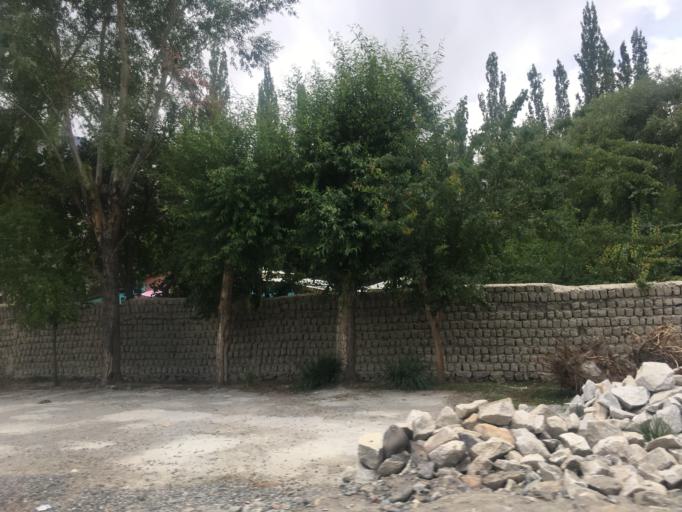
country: PK
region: Gilgit-Baltistan
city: Skardu
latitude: 35.2914
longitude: 75.6150
